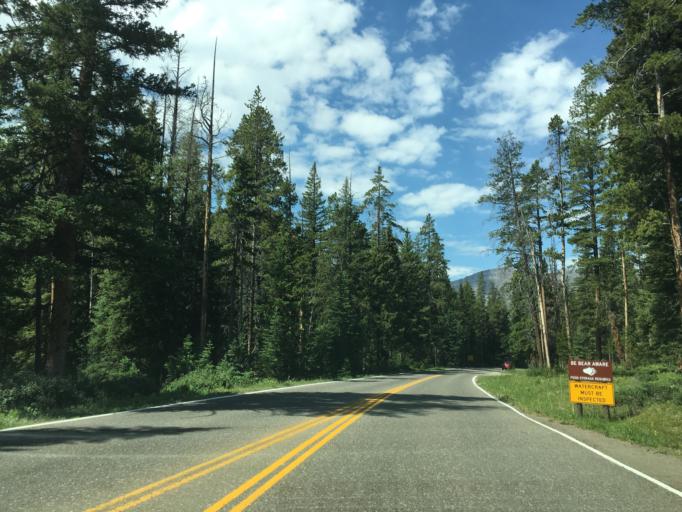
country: US
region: Montana
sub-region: Stillwater County
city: Absarokee
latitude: 45.0042
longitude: -110.0113
